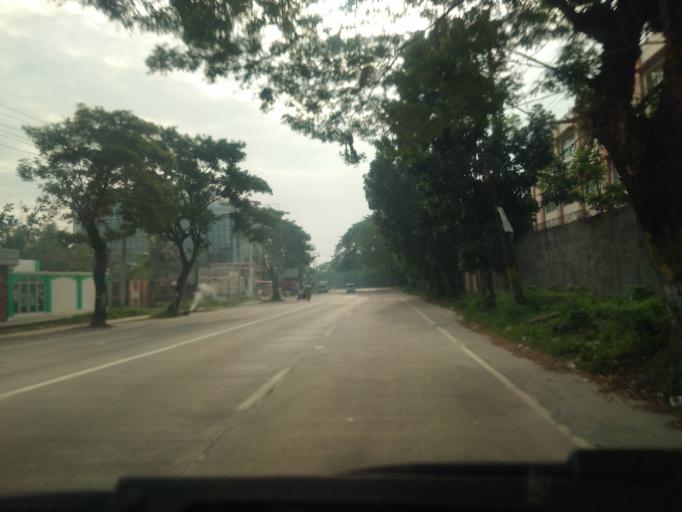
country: PH
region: Central Luzon
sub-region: Province of Pampanga
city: Angeles City
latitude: 15.1280
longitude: 120.5772
